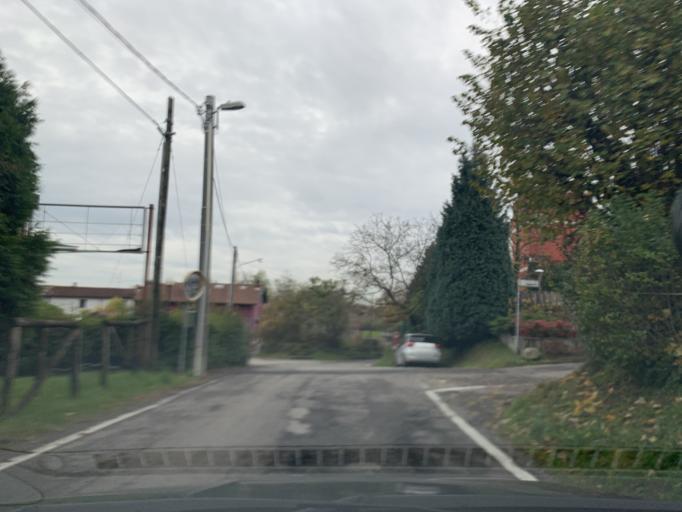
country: IT
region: Lombardy
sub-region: Provincia di Como
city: Casnate Con Bernate
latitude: 45.7480
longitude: 9.0703
